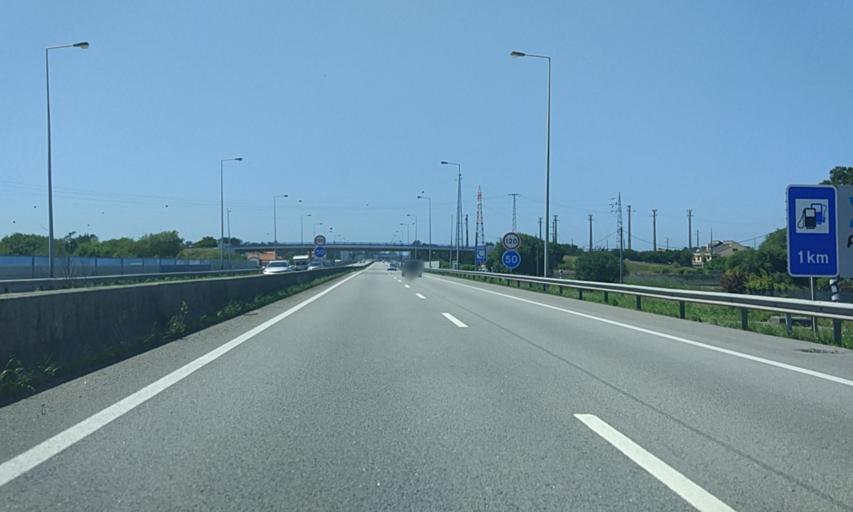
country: PT
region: Aveiro
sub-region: Ilhavo
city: Gafanha da Nazare
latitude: 40.6306
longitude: -8.6936
